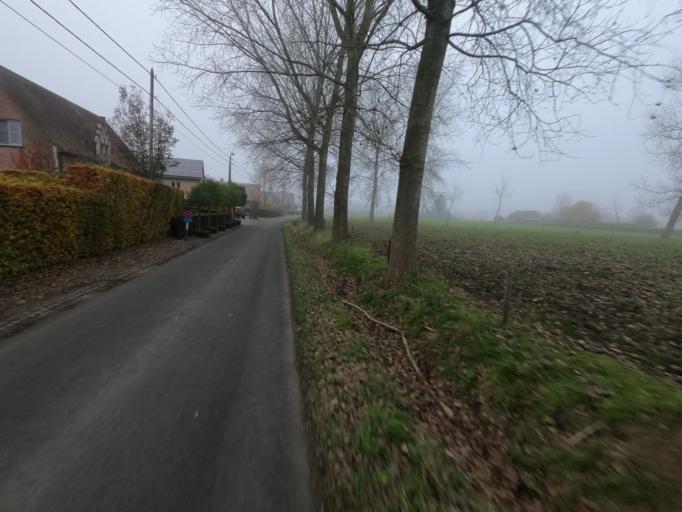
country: BE
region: Flanders
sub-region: Provincie Oost-Vlaanderen
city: Kruibeke
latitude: 51.1837
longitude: 4.2986
